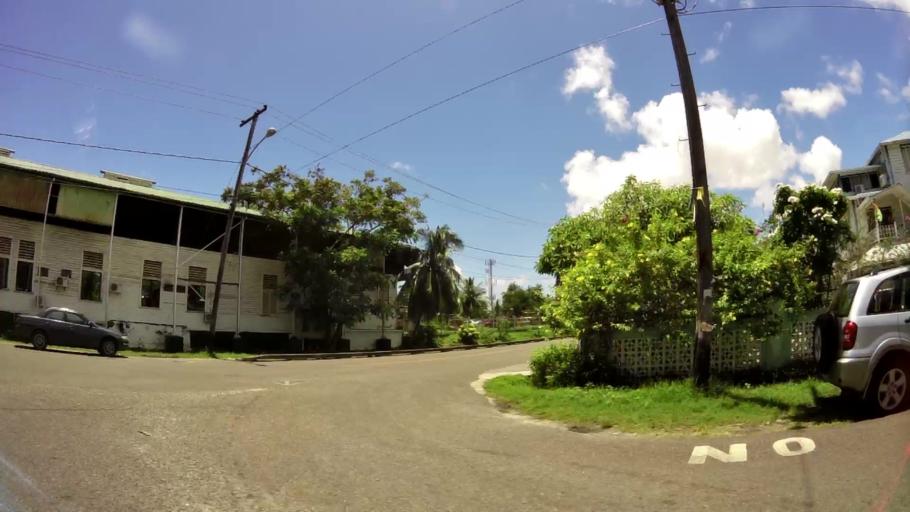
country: GY
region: Demerara-Mahaica
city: Georgetown
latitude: 6.8194
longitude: -58.1617
